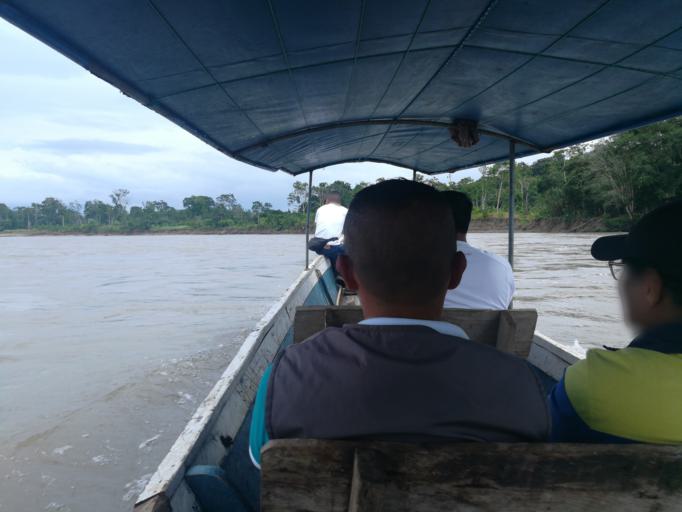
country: EC
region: Orellana
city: Boca Suno
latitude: -0.7696
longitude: -77.1802
